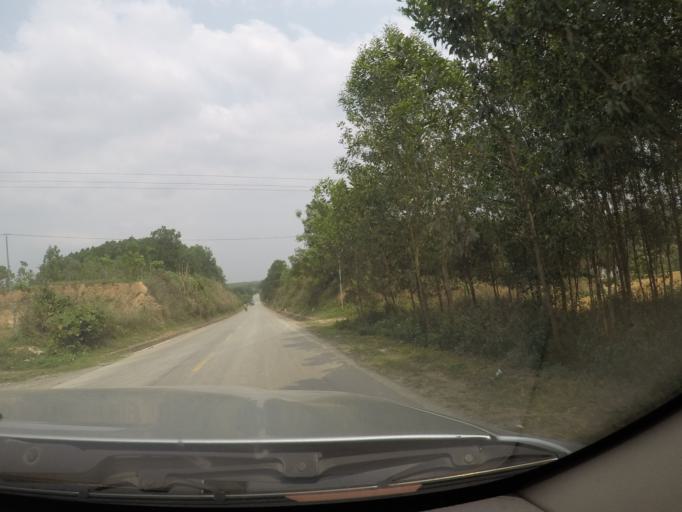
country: VN
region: Thanh Hoa
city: Thi Tran Yen Cat
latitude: 19.4748
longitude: 105.4206
